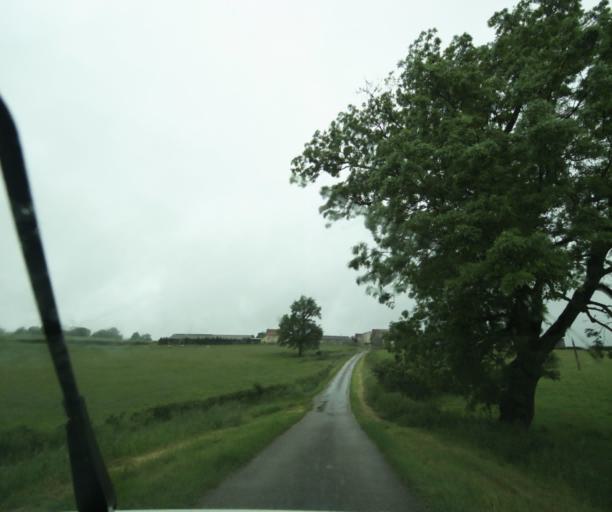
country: FR
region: Bourgogne
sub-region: Departement de Saone-et-Loire
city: Charolles
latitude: 46.4075
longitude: 4.2757
